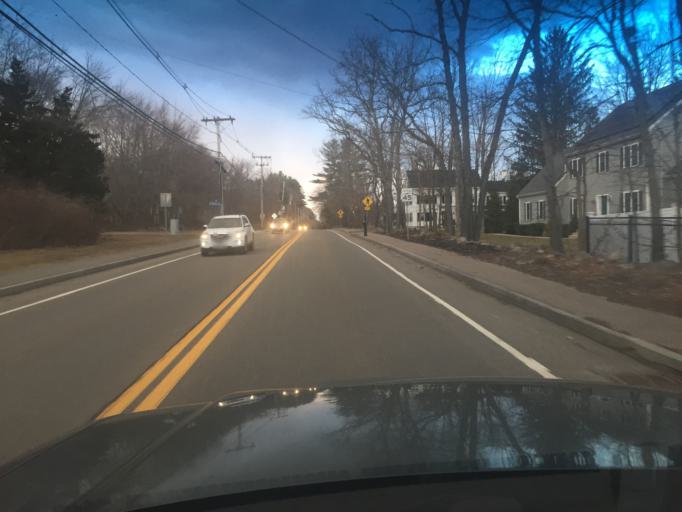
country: US
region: Massachusetts
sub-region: Middlesex County
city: Holliston
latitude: 42.1578
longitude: -71.4435
